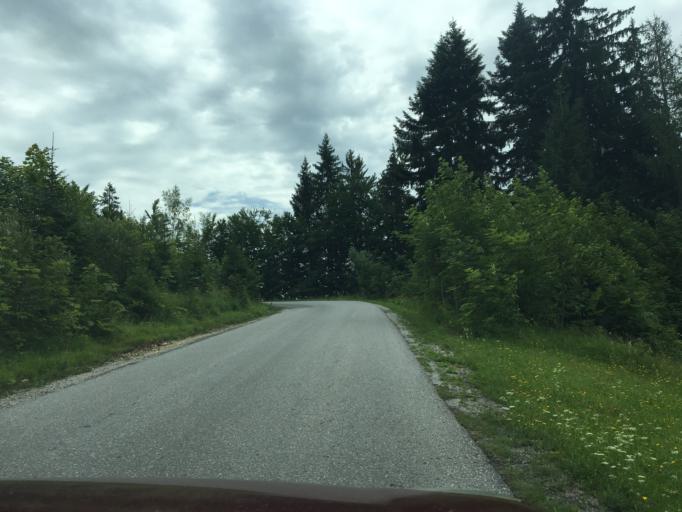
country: AT
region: Salzburg
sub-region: Politischer Bezirk Hallein
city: Abtenau
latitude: 47.6033
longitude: 13.3678
